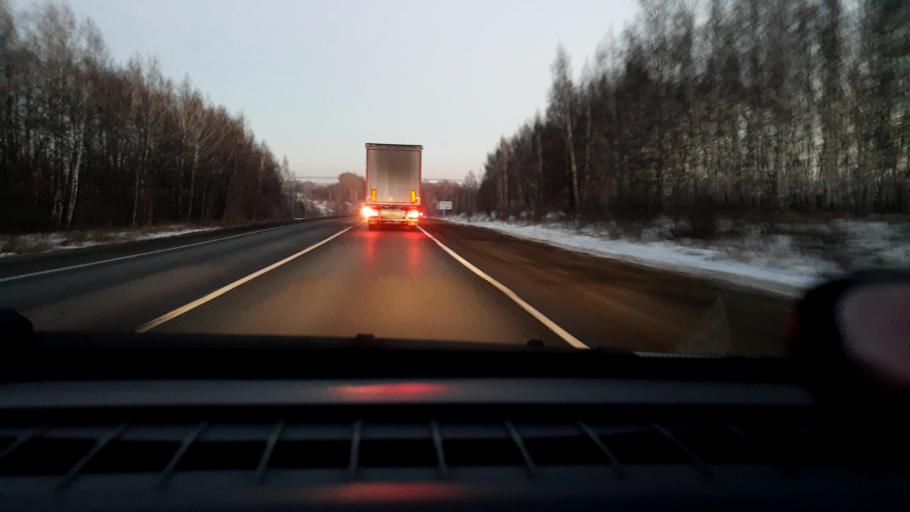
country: RU
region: Nizjnij Novgorod
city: Lyskovo
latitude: 56.0086
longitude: 44.8711
